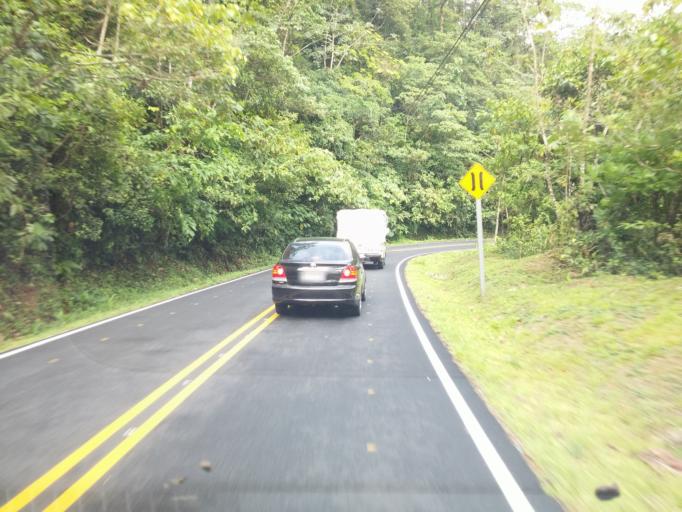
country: CR
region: Alajuela
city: San Ramon
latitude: 10.2163
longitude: -84.5429
